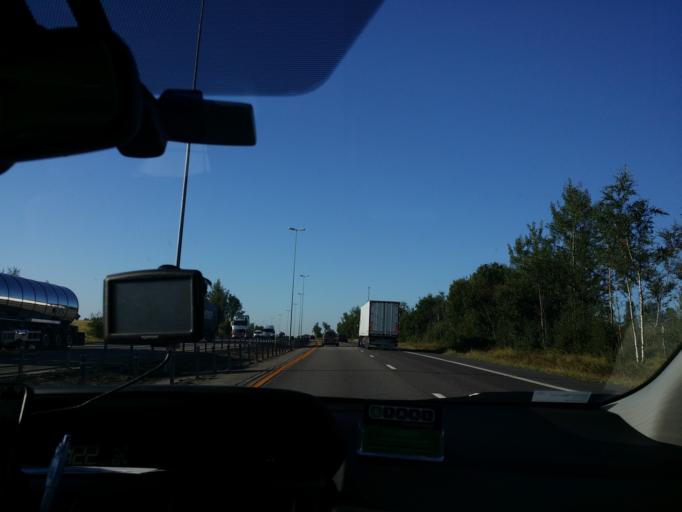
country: NO
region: Akershus
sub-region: Ullensaker
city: Klofta
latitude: 60.1045
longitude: 11.1435
